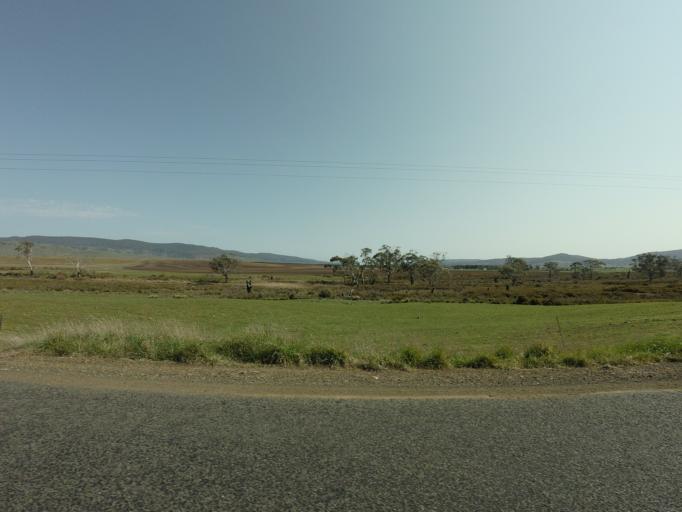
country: AU
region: Tasmania
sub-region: Northern Midlands
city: Evandale
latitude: -41.8051
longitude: 147.7527
